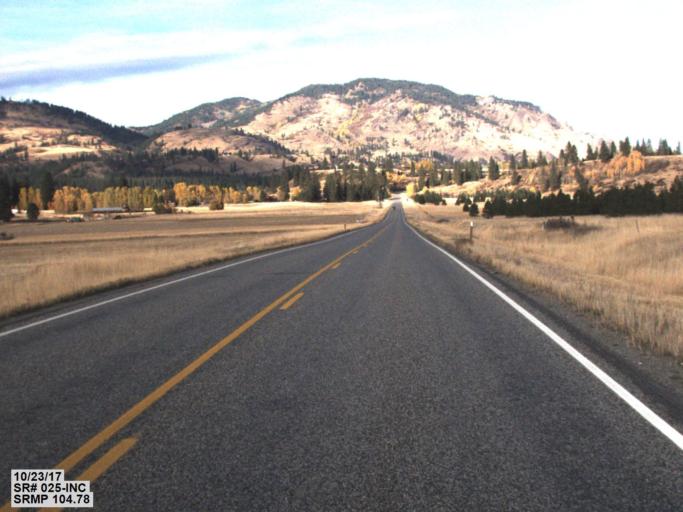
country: CA
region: British Columbia
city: Rossland
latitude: 48.8383
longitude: -117.9041
